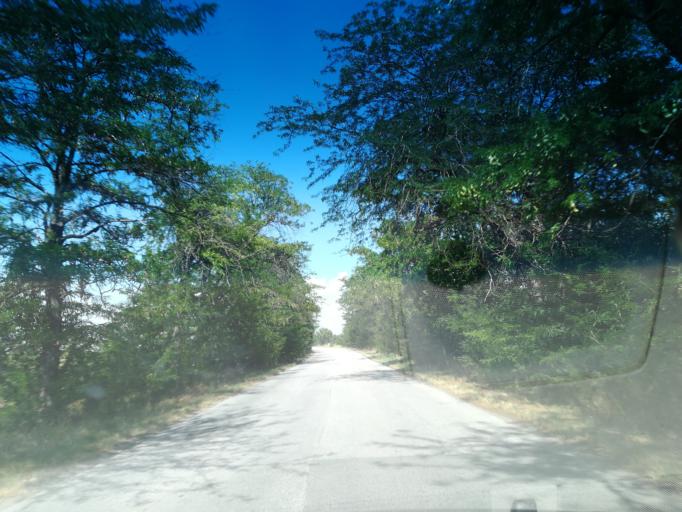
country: BG
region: Plovdiv
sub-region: Obshtina Sadovo
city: Sadovo
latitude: 42.0419
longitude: 25.1360
